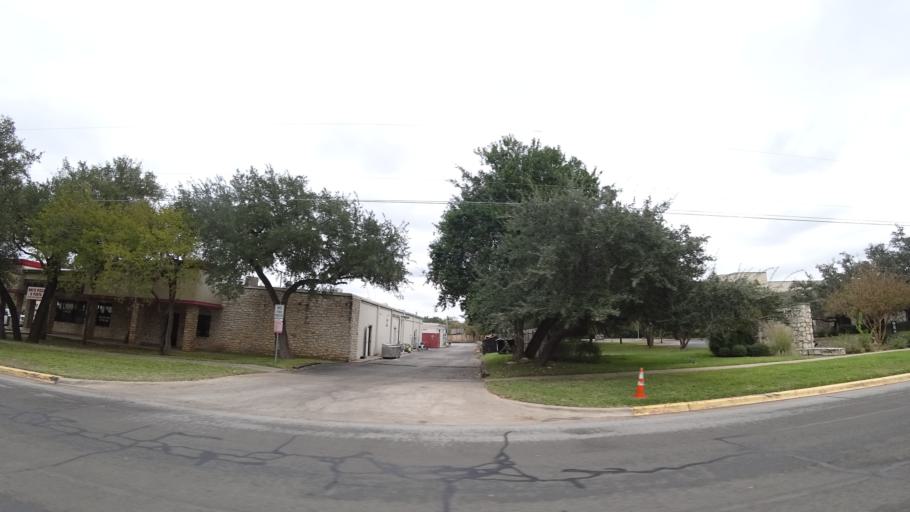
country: US
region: Texas
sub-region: Williamson County
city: Round Rock
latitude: 30.5099
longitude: -97.6949
